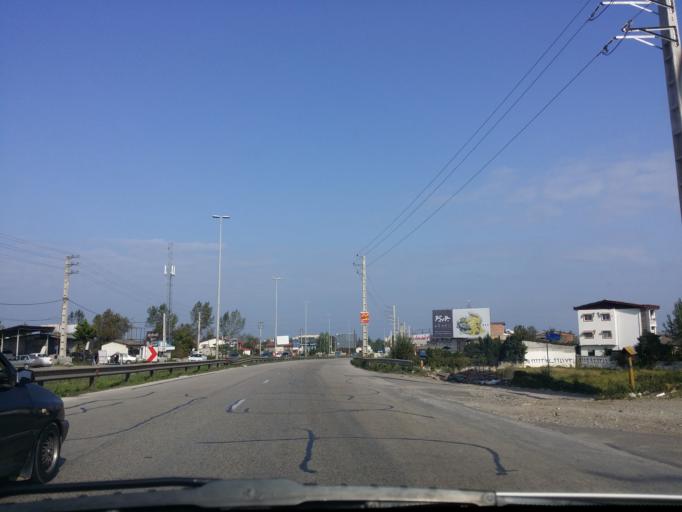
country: IR
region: Mazandaran
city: Chalus
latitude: 36.6695
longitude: 51.3959
